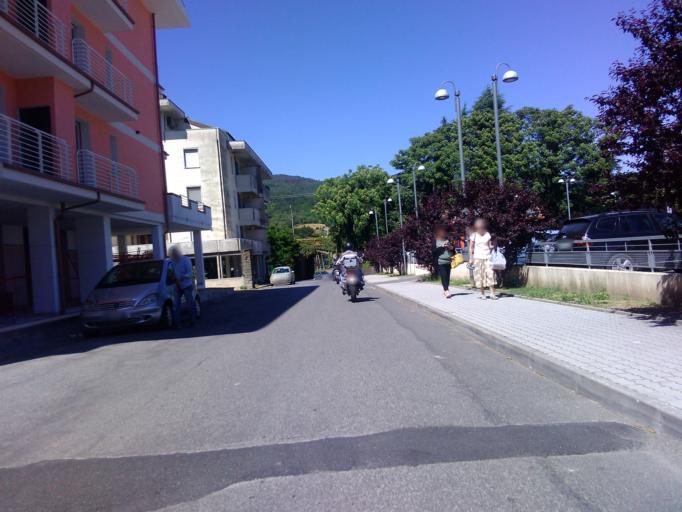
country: IT
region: Tuscany
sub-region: Provincia di Massa-Carrara
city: Villafranca in Lunigiana
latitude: 44.2934
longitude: 9.9495
